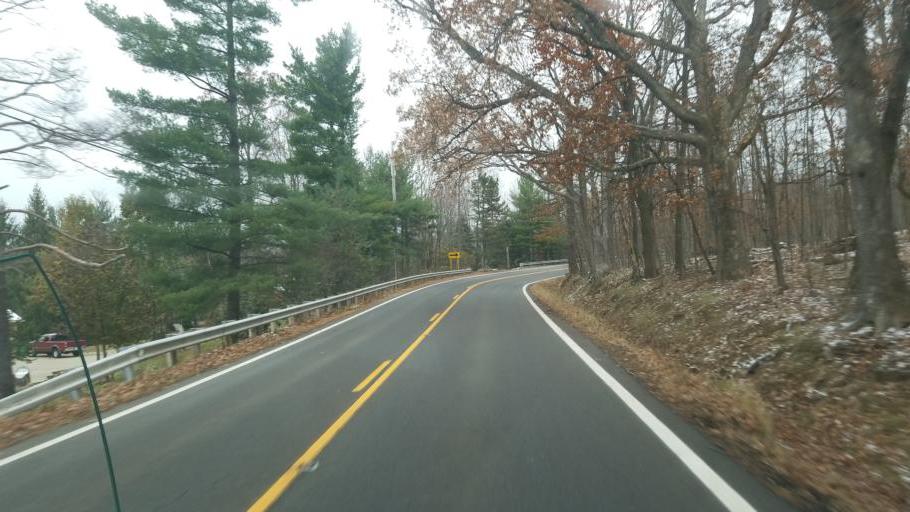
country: US
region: Ohio
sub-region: Cuyahoga County
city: North Royalton
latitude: 41.2736
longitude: -81.7251
